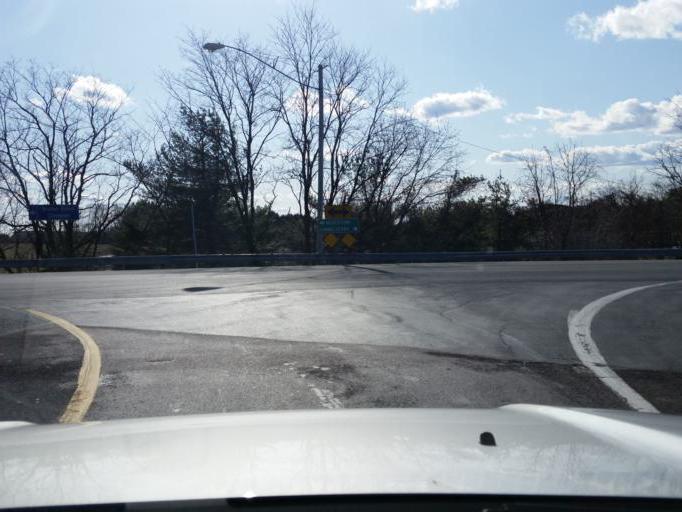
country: US
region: Pennsylvania
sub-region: Dauphin County
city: Hummelstown
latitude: 40.2594
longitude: -76.6998
